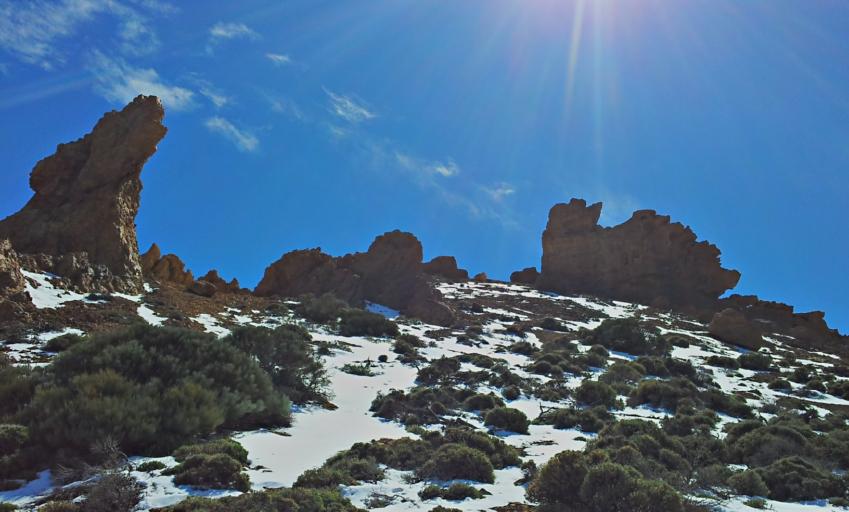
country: ES
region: Canary Islands
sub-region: Provincia de Santa Cruz de Tenerife
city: Vilaflor
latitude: 28.2268
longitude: -16.6346
